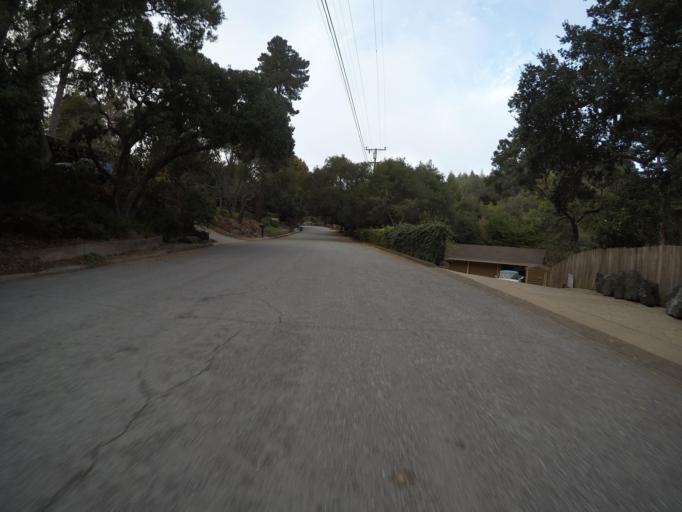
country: US
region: California
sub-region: Santa Cruz County
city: Pasatiempo
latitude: 37.0204
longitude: -122.0337
